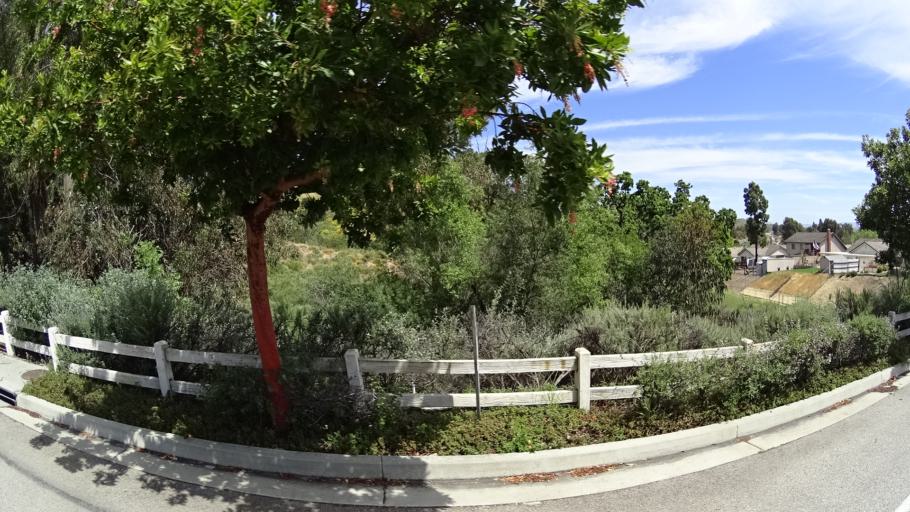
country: US
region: California
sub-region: Ventura County
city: Casa Conejo
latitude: 34.1794
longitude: -118.9620
